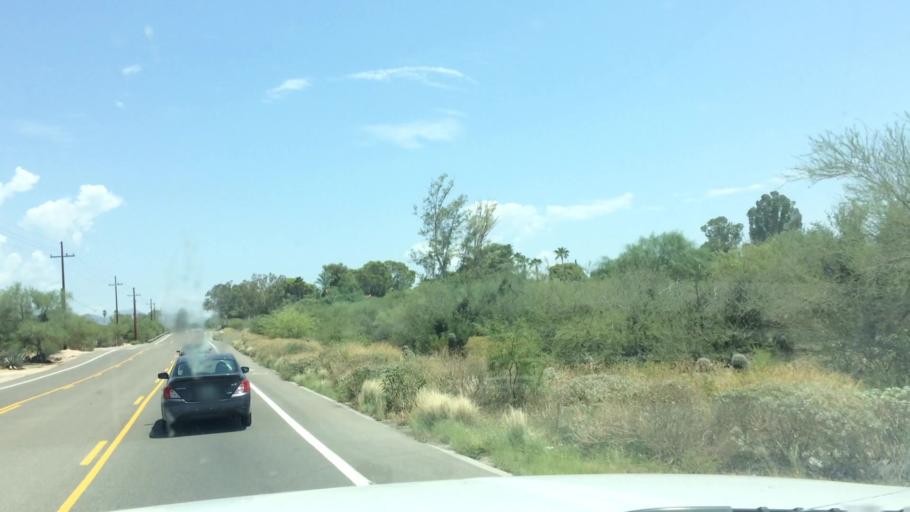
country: US
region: Arizona
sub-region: Pima County
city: Casas Adobes
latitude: 32.3231
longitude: -110.9892
